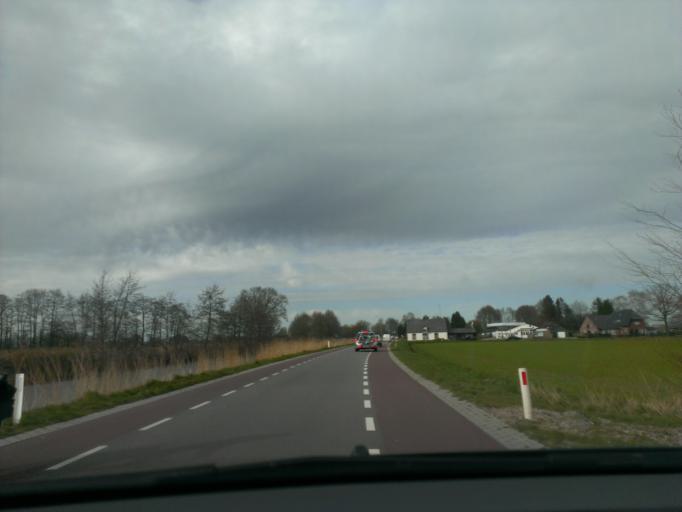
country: NL
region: Gelderland
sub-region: Gemeente Epe
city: Vaassen
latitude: 52.2525
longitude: 5.9808
